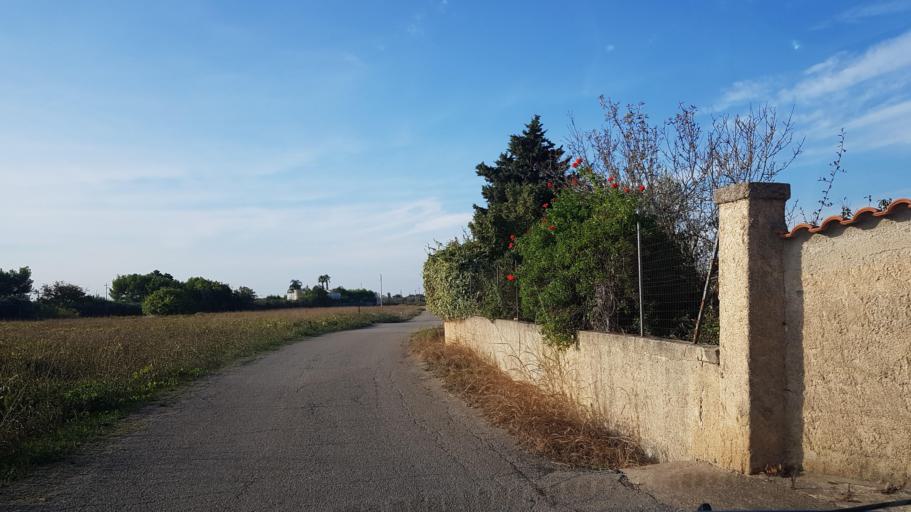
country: IT
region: Apulia
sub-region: Provincia di Brindisi
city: Mesagne
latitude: 40.5385
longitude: 17.8271
